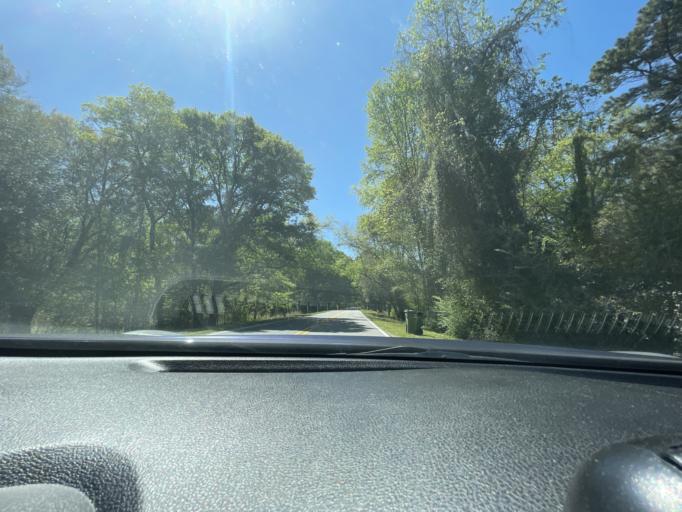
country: US
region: Georgia
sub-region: Chatham County
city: Pooler
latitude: 32.0909
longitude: -81.2430
